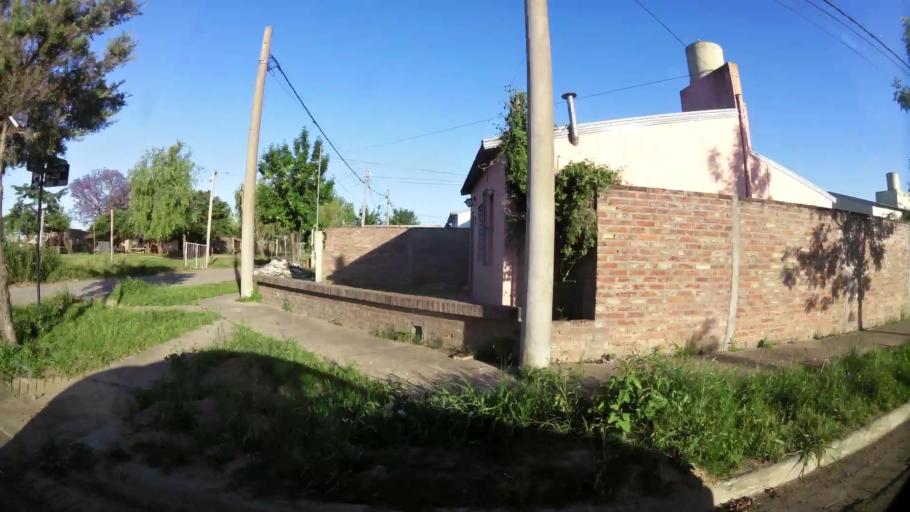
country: AR
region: Santa Fe
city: Santa Fe de la Vera Cruz
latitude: -31.5920
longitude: -60.6839
